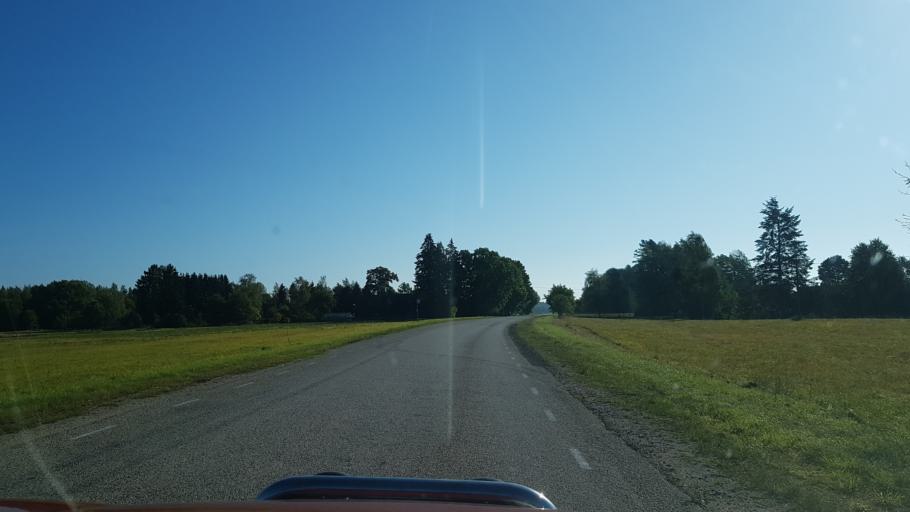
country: EE
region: Jogevamaa
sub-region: Tabivere vald
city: Tabivere
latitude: 58.6817
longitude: 26.6454
